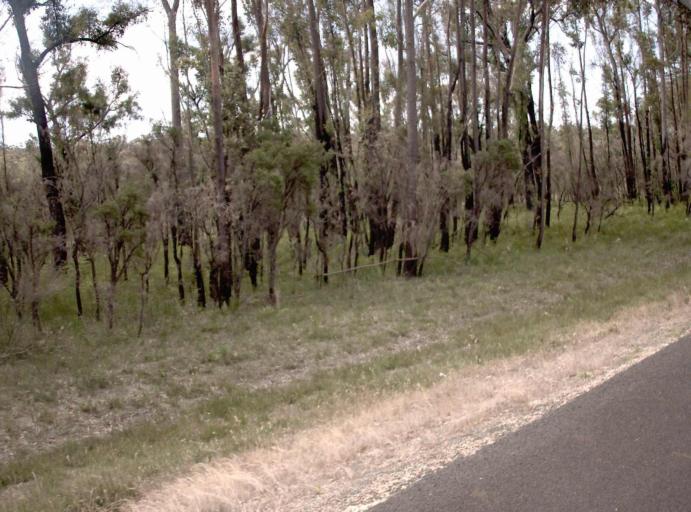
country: AU
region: New South Wales
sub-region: Bega Valley
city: Eden
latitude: -37.5152
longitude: 149.5026
